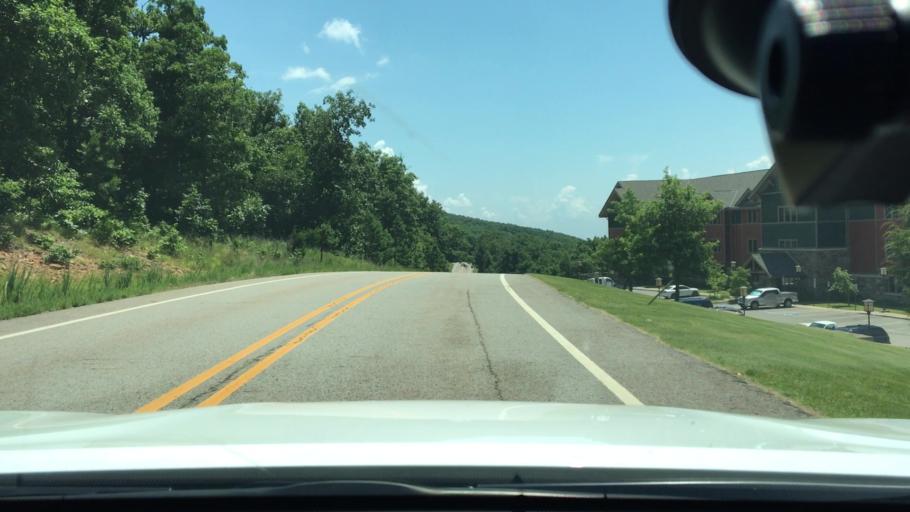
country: US
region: Arkansas
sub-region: Logan County
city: Paris
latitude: 35.1644
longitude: -93.6468
